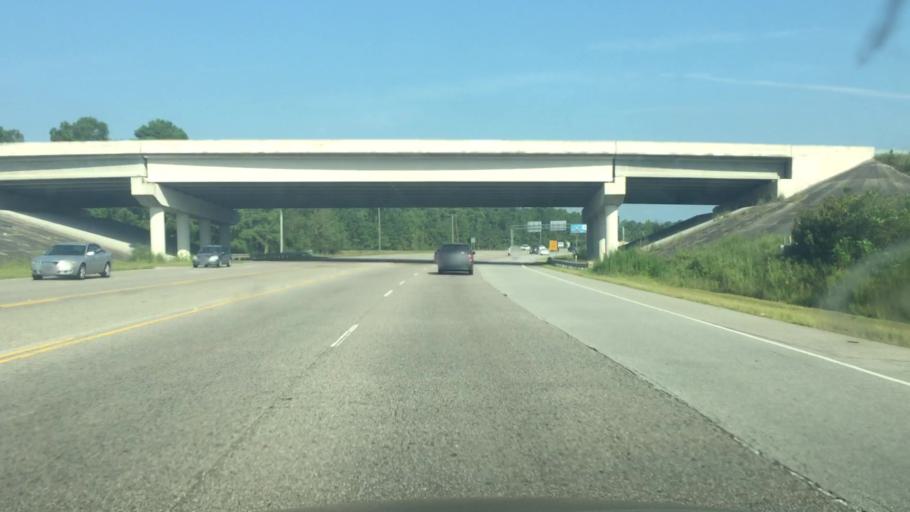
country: US
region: South Carolina
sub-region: Horry County
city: North Myrtle Beach
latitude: 33.8753
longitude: -78.6814
